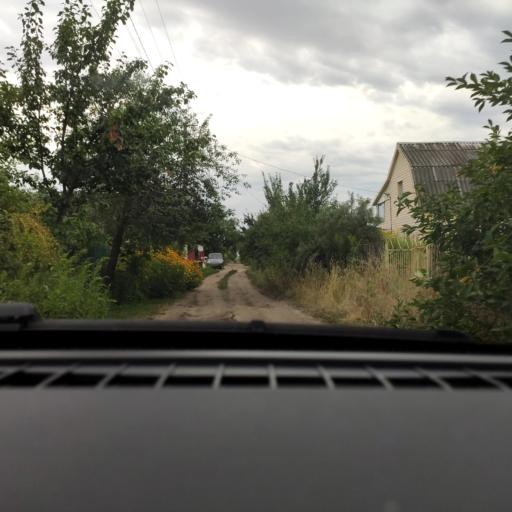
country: RU
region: Voronezj
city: Maslovka
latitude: 51.5204
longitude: 39.2346
